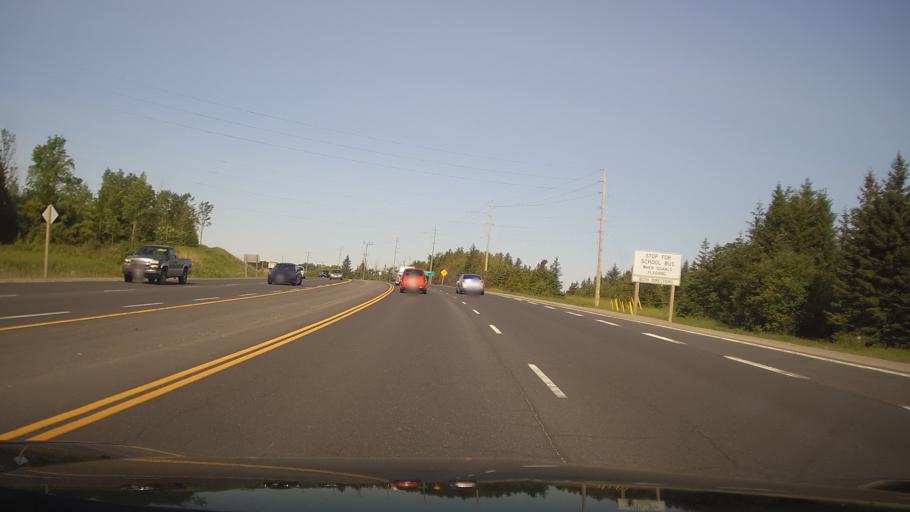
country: CA
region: Ontario
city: Peterborough
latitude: 44.3172
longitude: -78.2031
